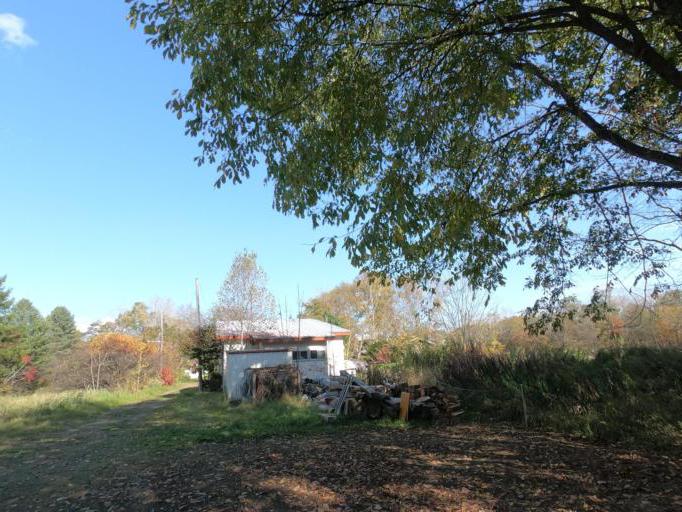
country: JP
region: Hokkaido
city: Otofuke
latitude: 43.2332
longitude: 143.2625
